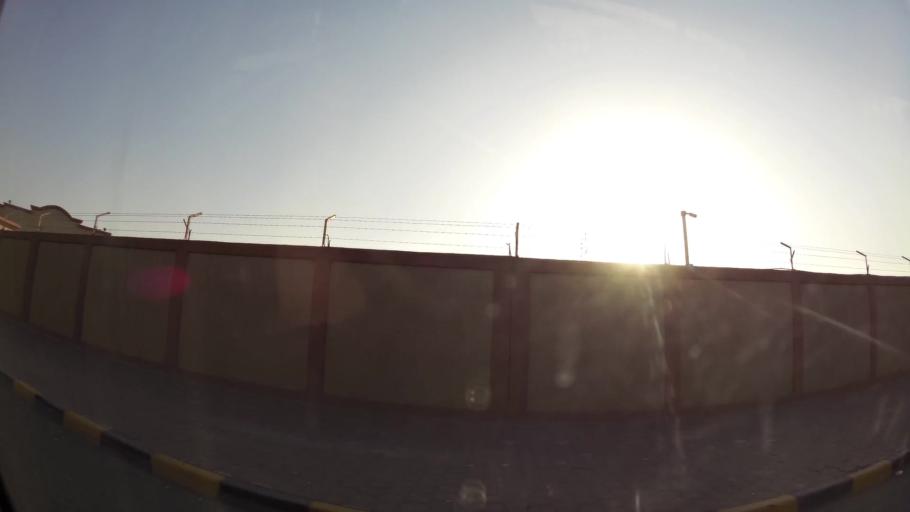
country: KW
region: Muhafazat Hawalli
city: As Salimiyah
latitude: 29.3276
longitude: 48.0760
